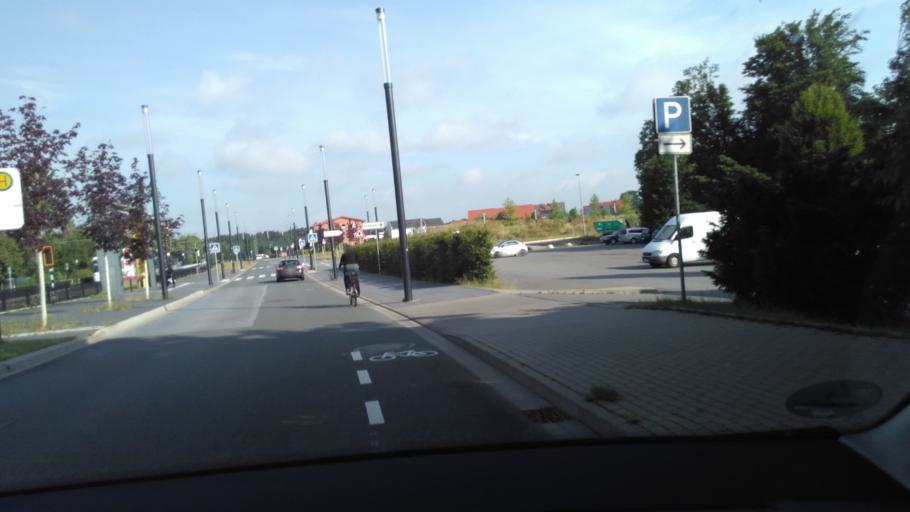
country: DE
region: North Rhine-Westphalia
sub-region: Regierungsbezirk Detmold
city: Bielefeld
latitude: 52.0416
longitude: 8.4917
